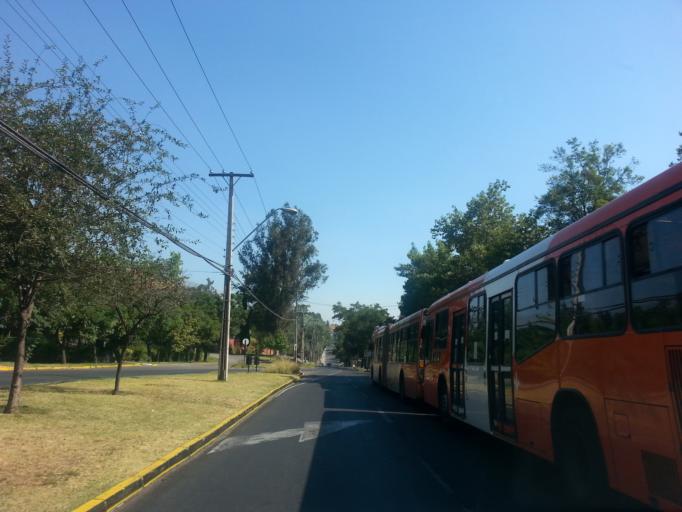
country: CL
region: Santiago Metropolitan
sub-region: Provincia de Santiago
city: Villa Presidente Frei, Nunoa, Santiago, Chile
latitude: -33.4177
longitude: -70.5297
